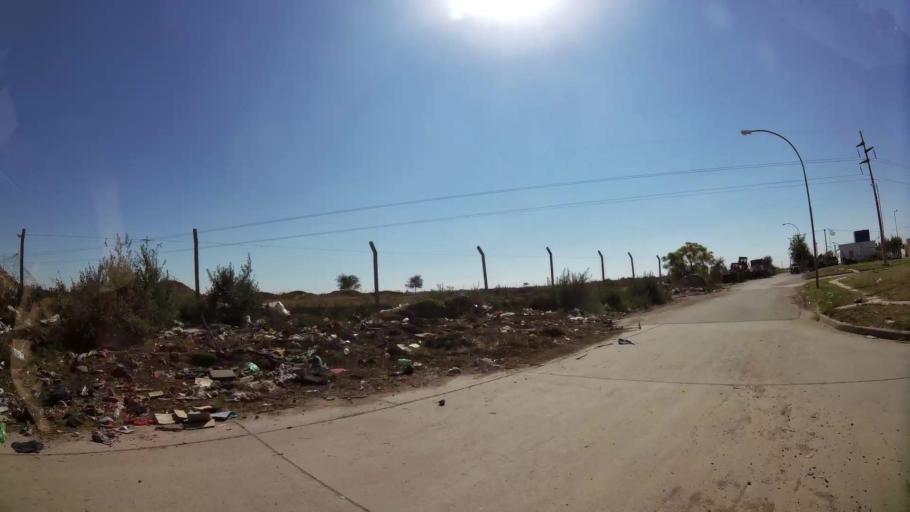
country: AR
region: Cordoba
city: Villa Allende
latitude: -31.3206
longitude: -64.2440
